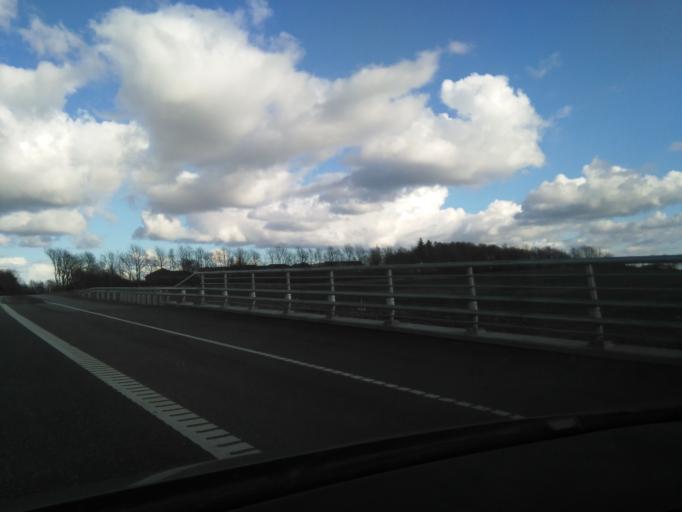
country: DK
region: Central Jutland
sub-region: Silkeborg Kommune
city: Silkeborg
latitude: 56.1897
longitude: 9.4951
